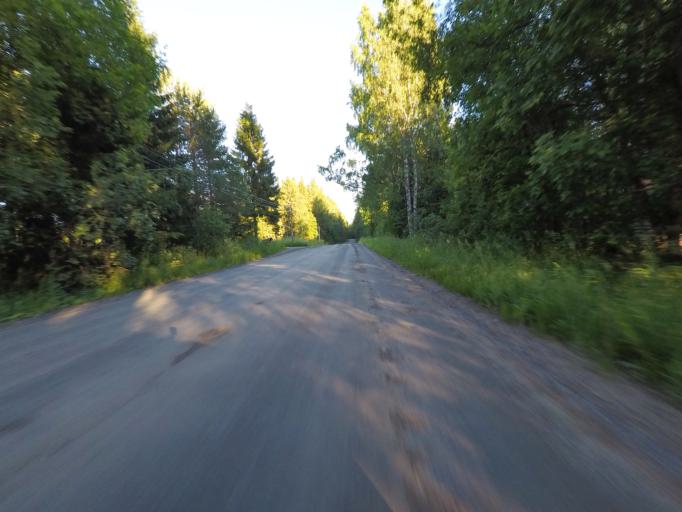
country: FI
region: Northern Savo
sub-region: Kuopio
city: Maaninka
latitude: 62.8608
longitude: 27.3240
